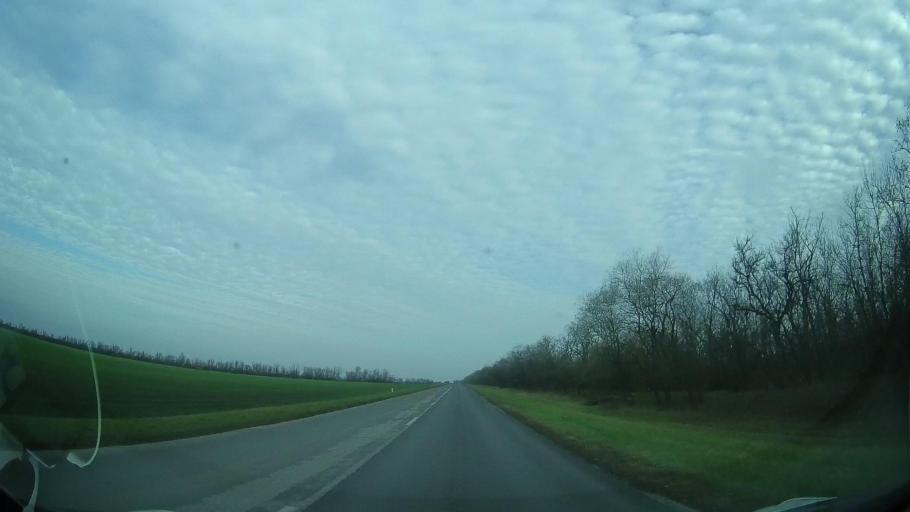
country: RU
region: Rostov
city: Zernograd
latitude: 46.9252
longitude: 40.3466
